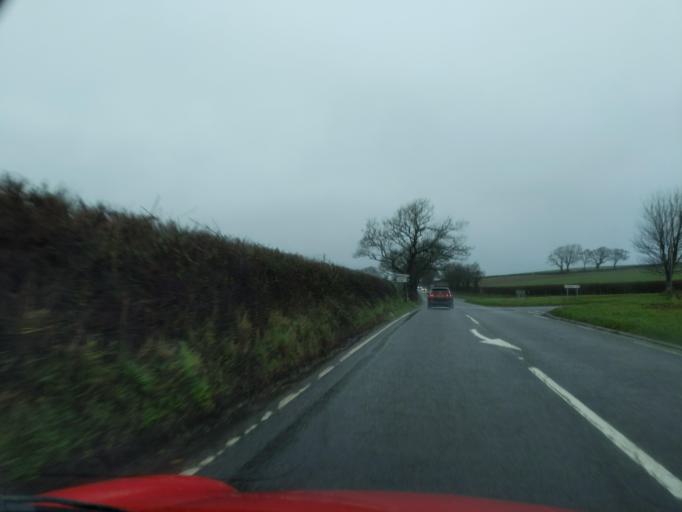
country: GB
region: England
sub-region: Cornwall
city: Launceston
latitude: 50.6151
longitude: -4.3399
